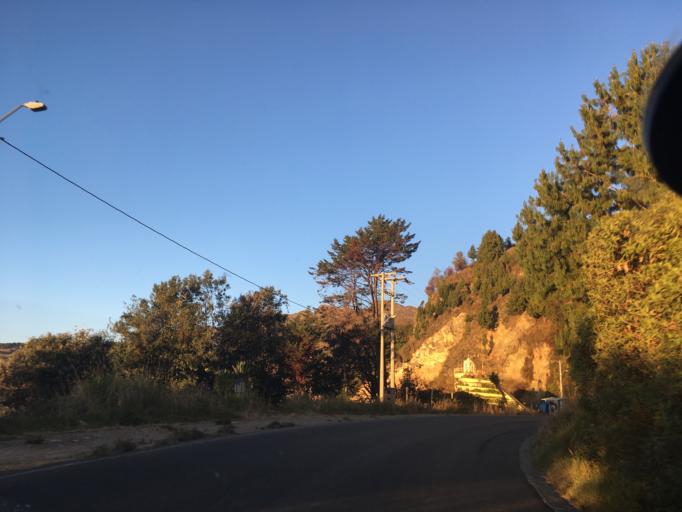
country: CO
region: Boyaca
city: Aquitania
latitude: 5.5483
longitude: -72.8830
